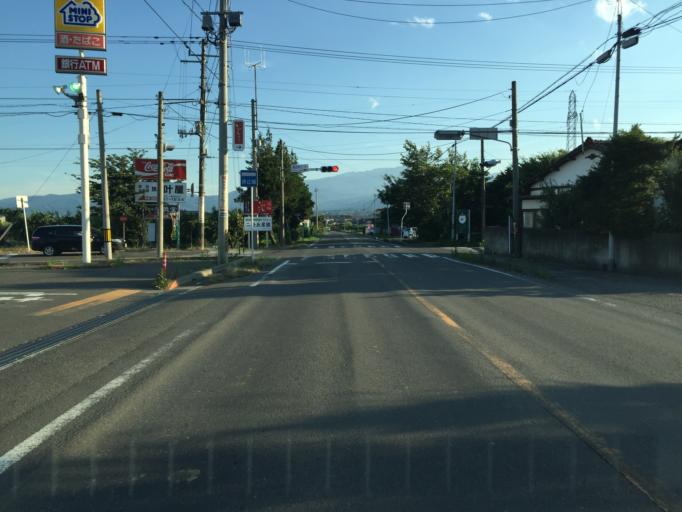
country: JP
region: Fukushima
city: Fukushima-shi
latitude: 37.7766
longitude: 140.3879
